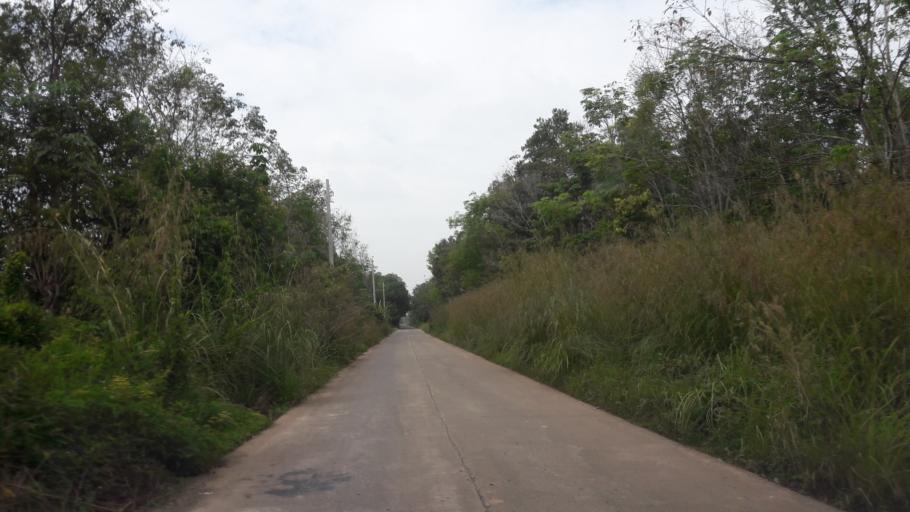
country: ID
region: South Sumatra
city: Gunungmenang
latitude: -3.2479
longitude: 104.1381
